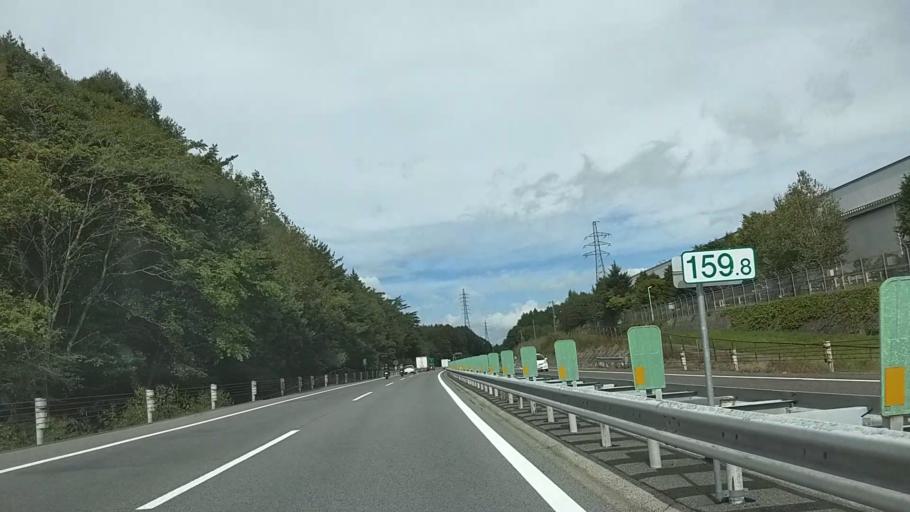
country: JP
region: Nagano
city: Chino
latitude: 35.9307
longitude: 138.2180
